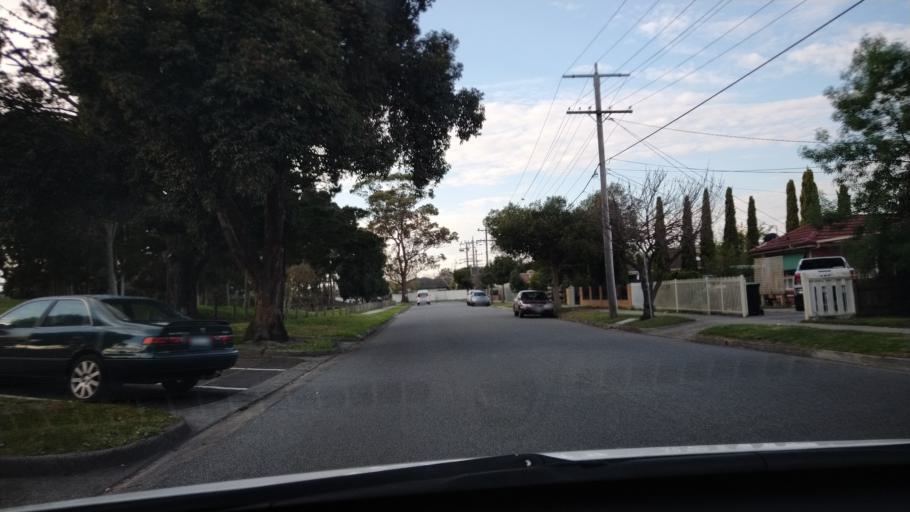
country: AU
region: Victoria
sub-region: Greater Dandenong
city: Springvale South
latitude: -37.9641
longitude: 145.1546
